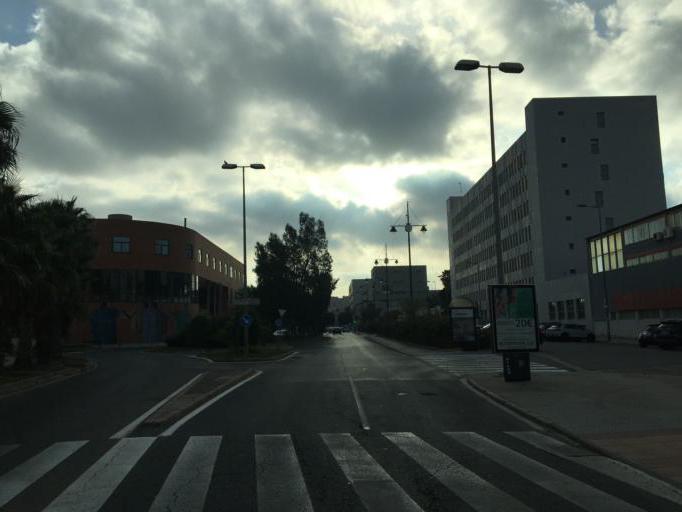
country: ES
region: Murcia
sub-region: Murcia
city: Cartagena
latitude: 37.6091
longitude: -0.9800
